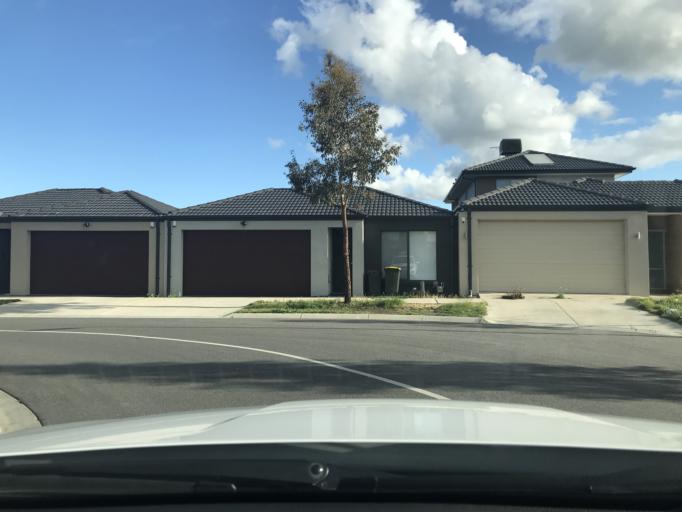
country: AU
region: Victoria
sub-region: Hume
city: Roxburgh Park
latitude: -37.5886
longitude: 144.8962
